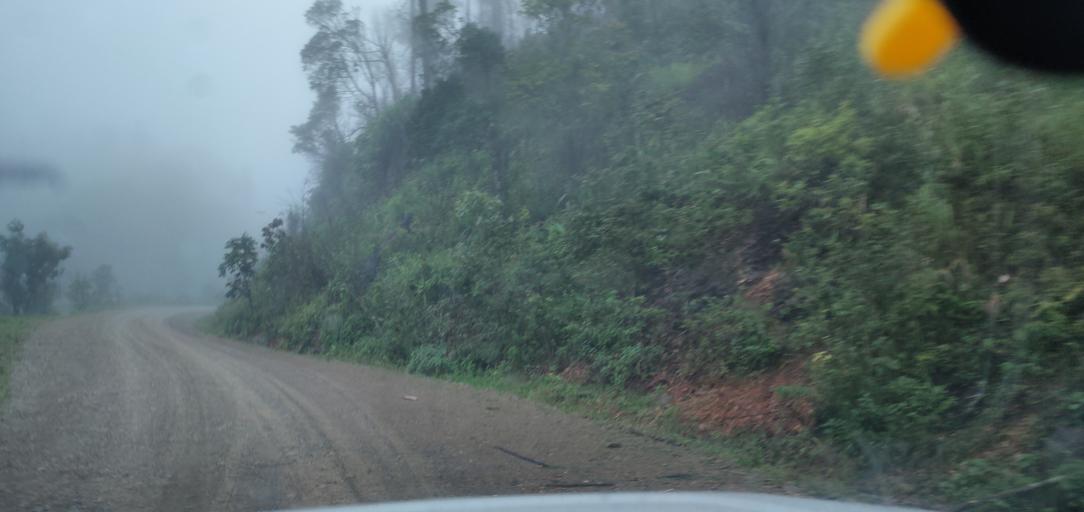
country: LA
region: Phongsali
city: Phongsali
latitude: 21.3952
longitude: 102.1922
